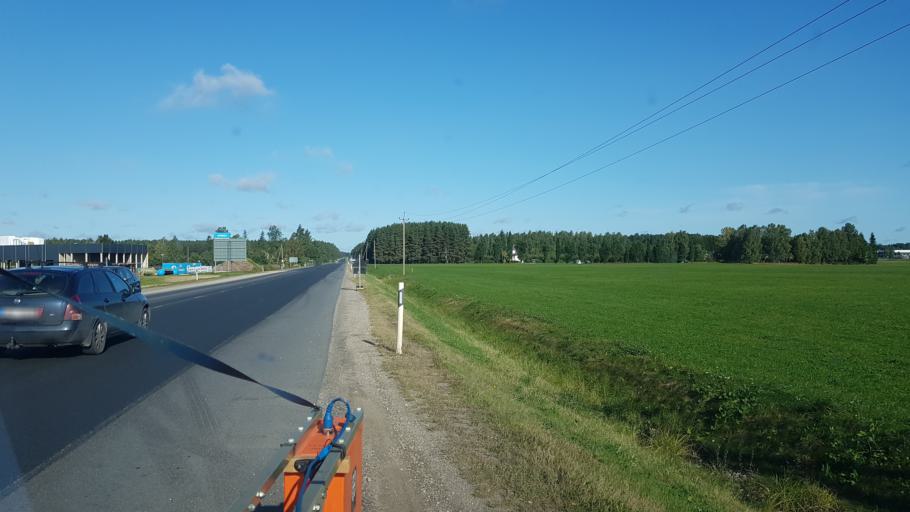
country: EE
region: Tartu
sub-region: Tartu linn
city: Tartu
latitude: 58.3830
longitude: 26.6778
